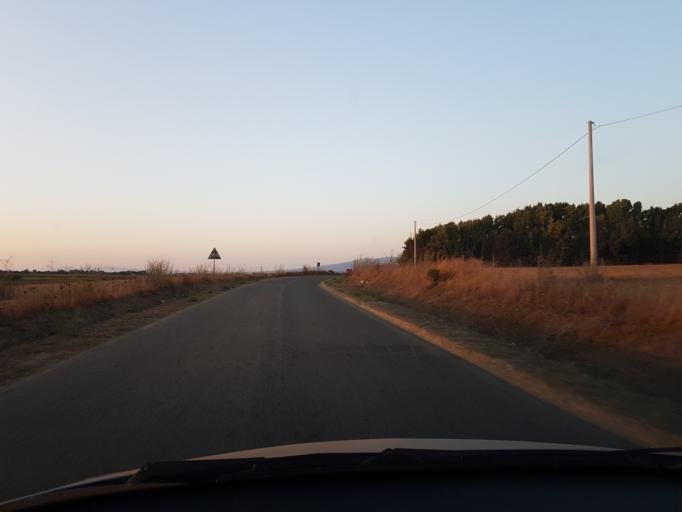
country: IT
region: Sardinia
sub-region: Provincia di Oristano
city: Nurachi
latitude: 39.9876
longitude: 8.4590
